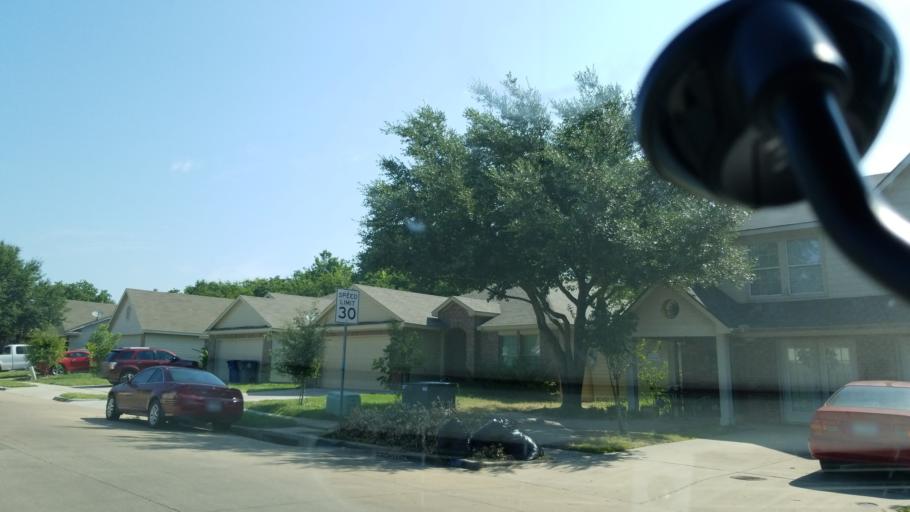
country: US
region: Texas
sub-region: Dallas County
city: Cockrell Hill
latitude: 32.7107
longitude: -96.8731
